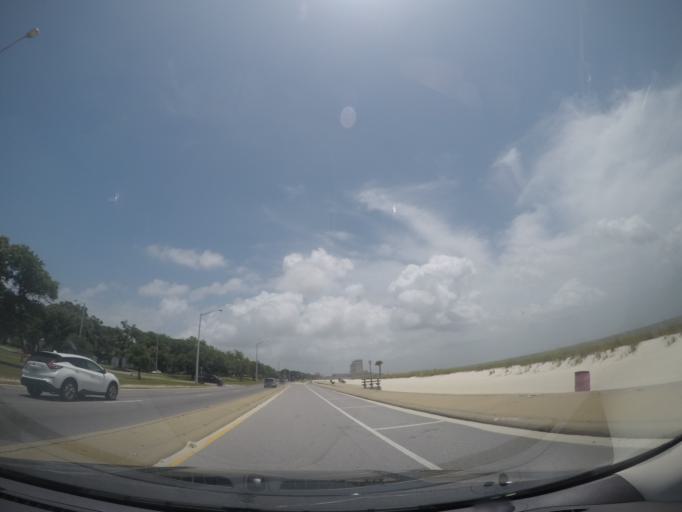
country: US
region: Mississippi
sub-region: Harrison County
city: Biloxi
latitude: 30.3944
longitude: -88.9095
